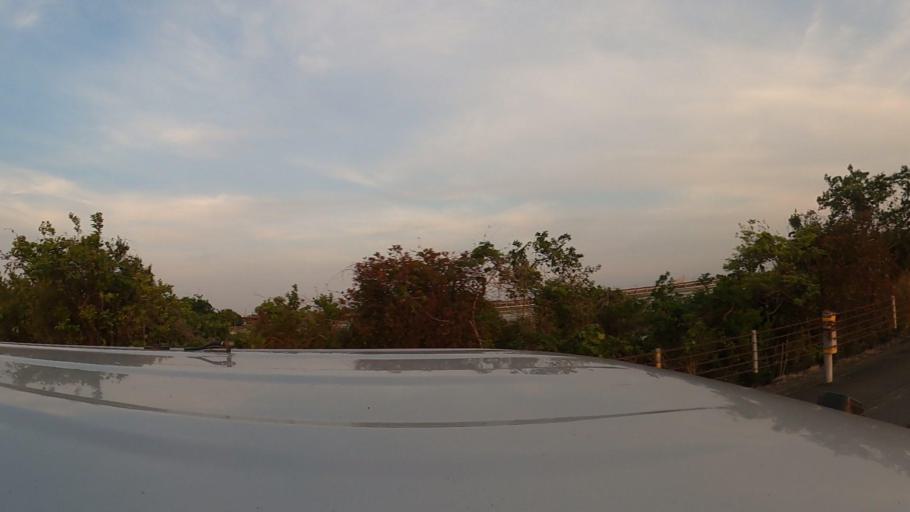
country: JP
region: Ibaraki
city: Mitsukaido
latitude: 35.9911
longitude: 140.0292
